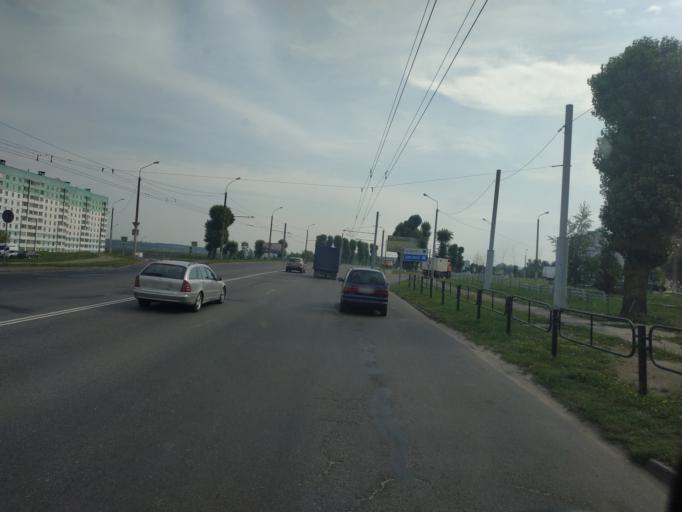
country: BY
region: Mogilev
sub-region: Mahilyowski Rayon
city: Veyno
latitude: 53.8768
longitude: 30.3803
